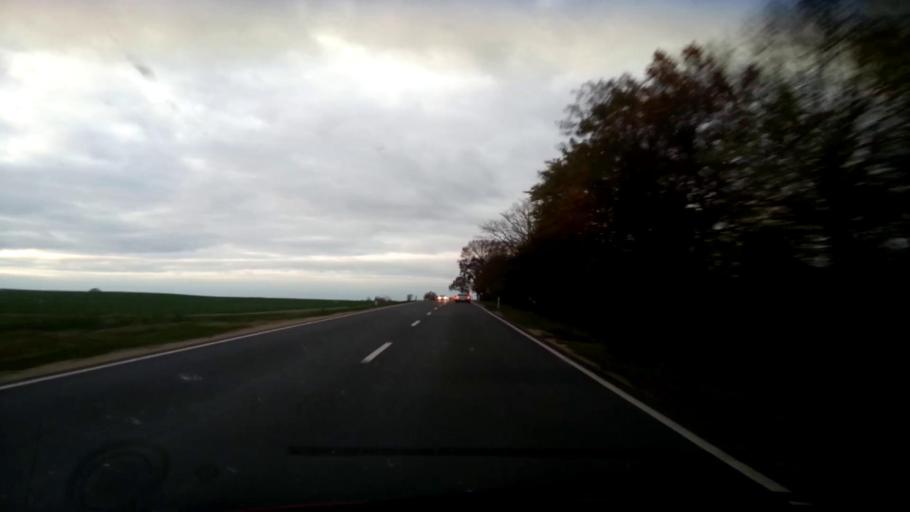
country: DE
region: Bavaria
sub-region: Upper Franconia
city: Sonnefeld
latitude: 50.2179
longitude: 11.0627
